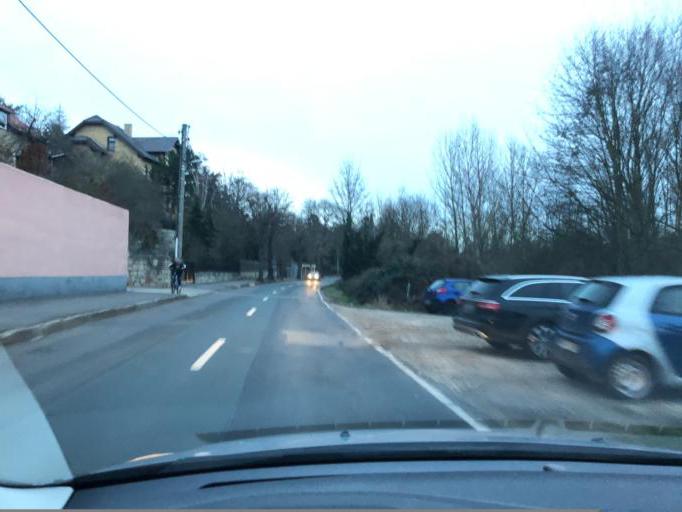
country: DE
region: Saxony-Anhalt
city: Weissenfels
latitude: 51.2150
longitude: 11.9537
